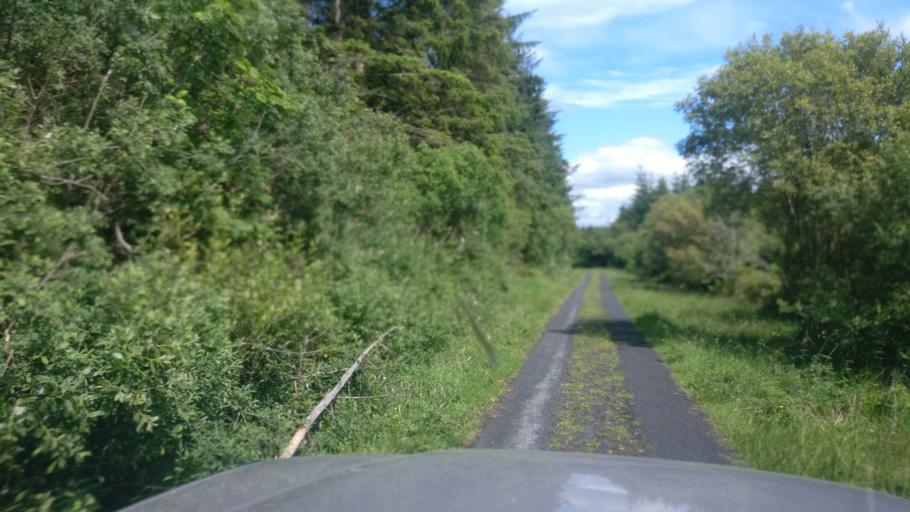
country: IE
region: Connaught
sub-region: County Galway
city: Gort
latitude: 53.0636
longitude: -8.6871
